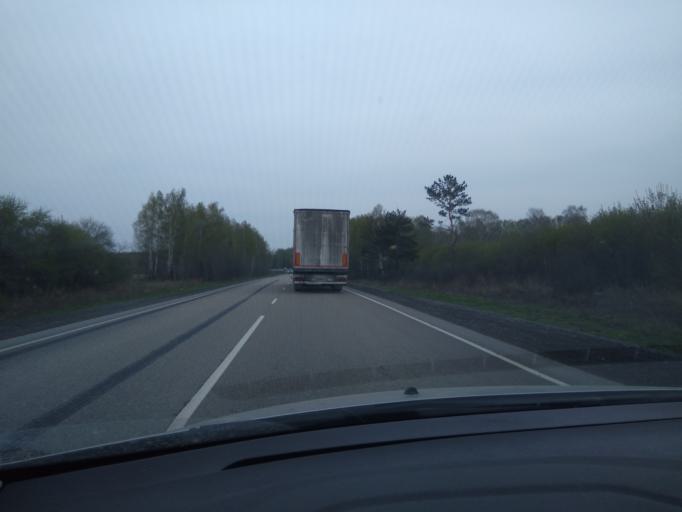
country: RU
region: Sverdlovsk
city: Zarechnyy
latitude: 56.7435
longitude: 61.2808
